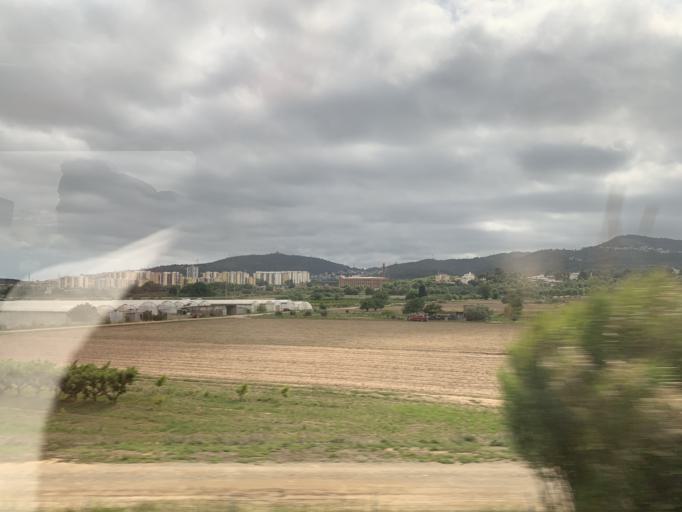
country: ES
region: Catalonia
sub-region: Provincia de Barcelona
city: Sant Feliu de Llobregat
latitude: 41.3668
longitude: 2.0376
